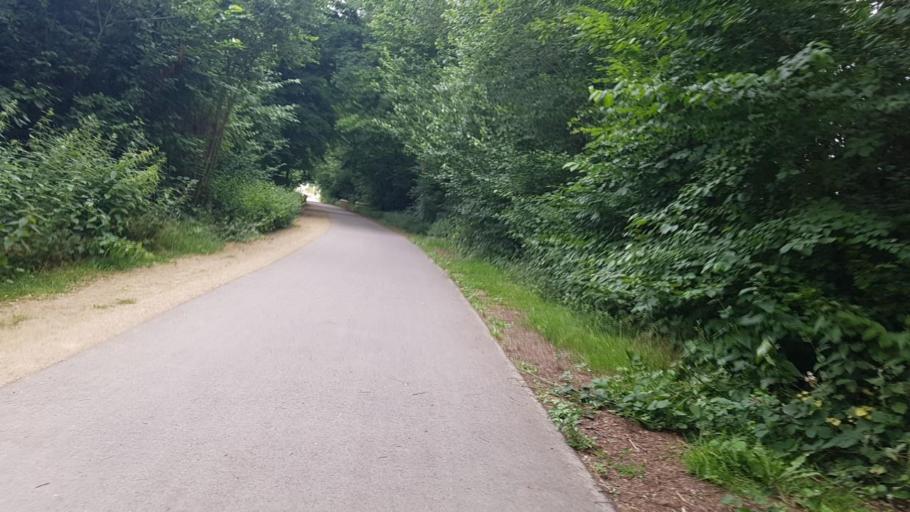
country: BE
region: Wallonia
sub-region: Province de Liege
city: Plombieres
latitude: 50.7445
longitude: 5.9904
